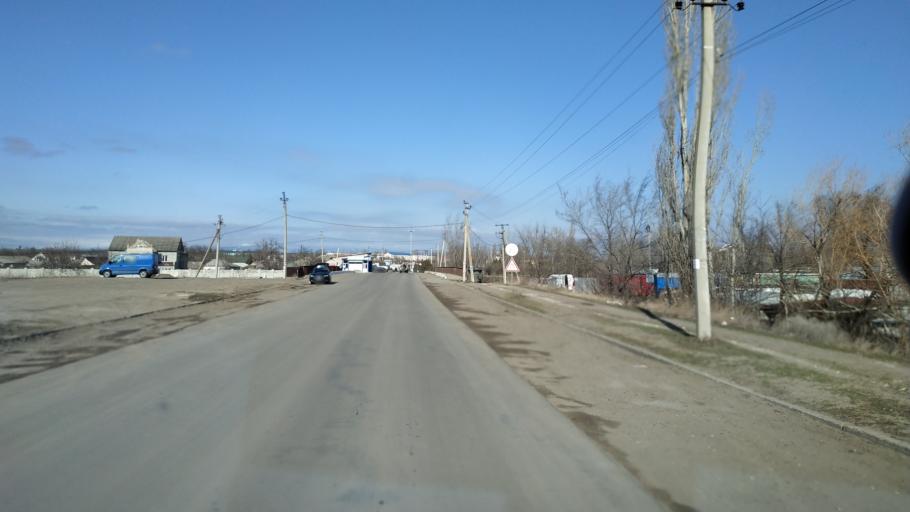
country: MD
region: Causeni
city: Causeni
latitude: 46.6467
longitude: 29.4056
